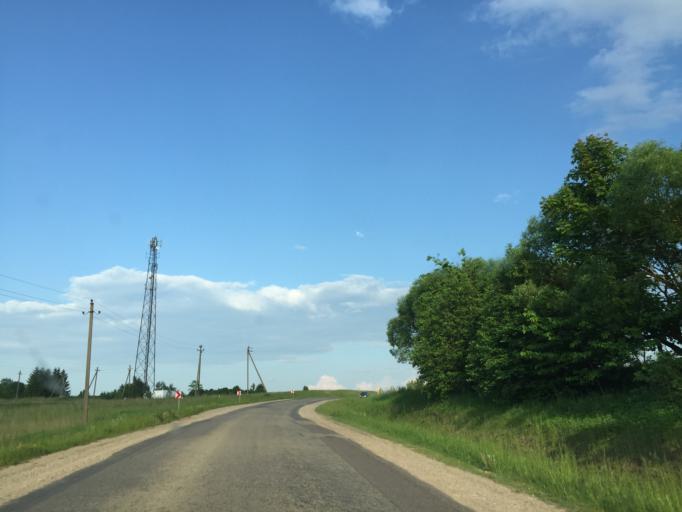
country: LT
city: Plateliai
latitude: 56.0462
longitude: 21.8027
